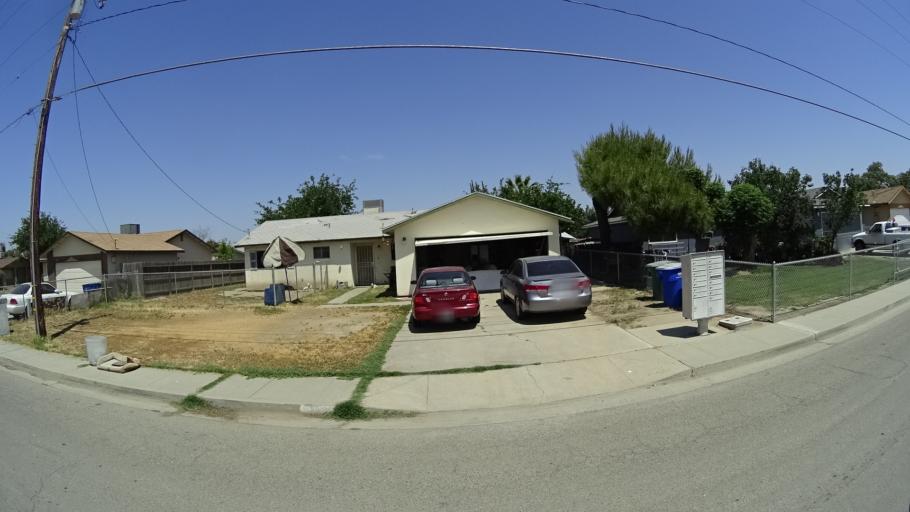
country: US
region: California
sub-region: Kings County
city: Armona
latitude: 36.3058
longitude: -119.7100
